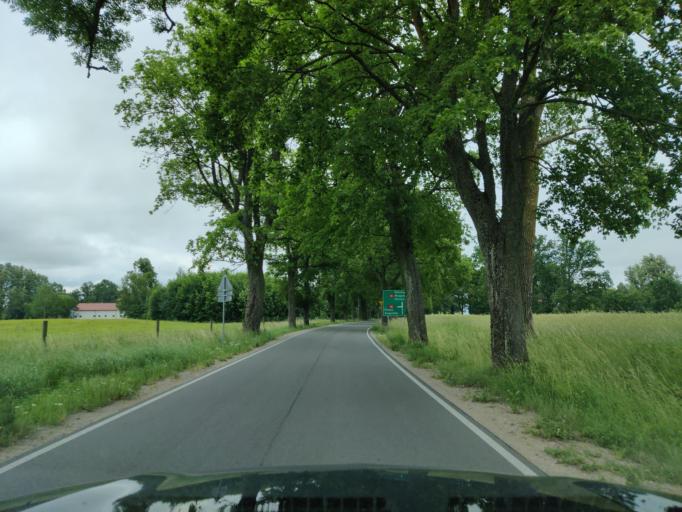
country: PL
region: Warmian-Masurian Voivodeship
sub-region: Powiat mragowski
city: Mikolajki
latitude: 53.8545
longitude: 21.6135
